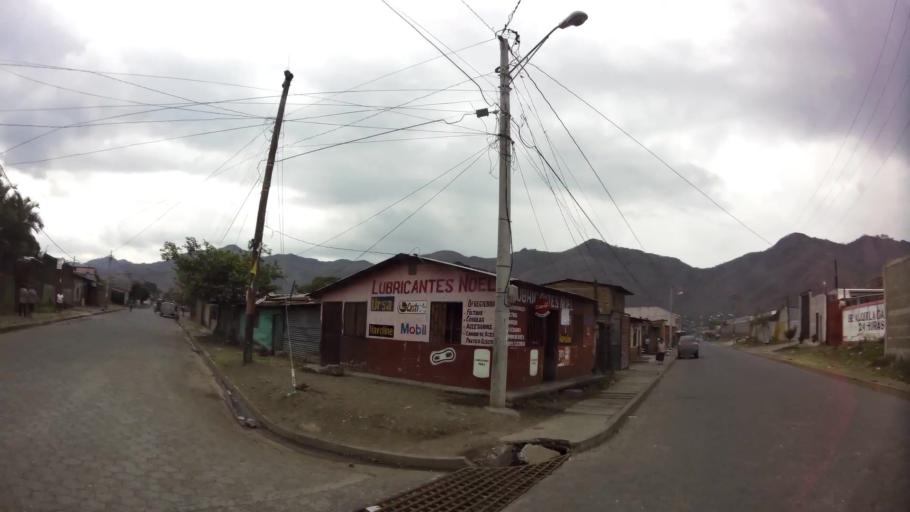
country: NI
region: Jinotega
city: Jinotega
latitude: 13.0977
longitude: -85.9984
